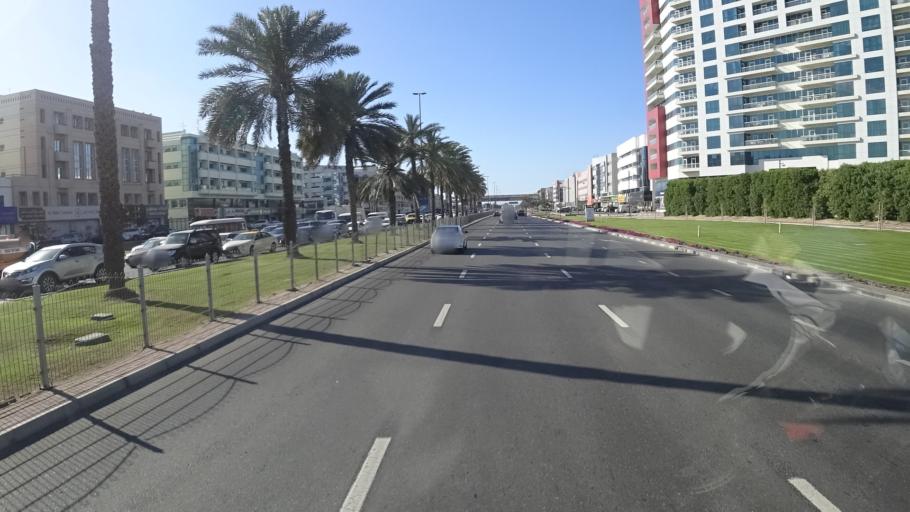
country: AE
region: Ash Shariqah
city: Sharjah
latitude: 25.2817
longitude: 55.3553
